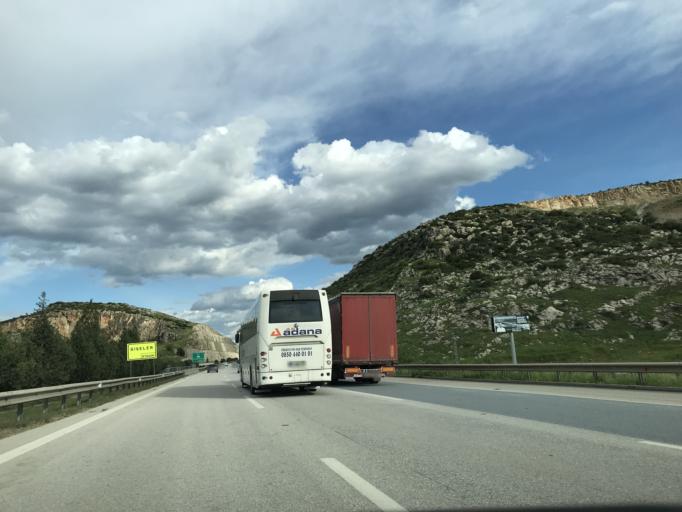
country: TR
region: Adana
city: Ceyhan
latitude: 37.0006
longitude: 35.7297
